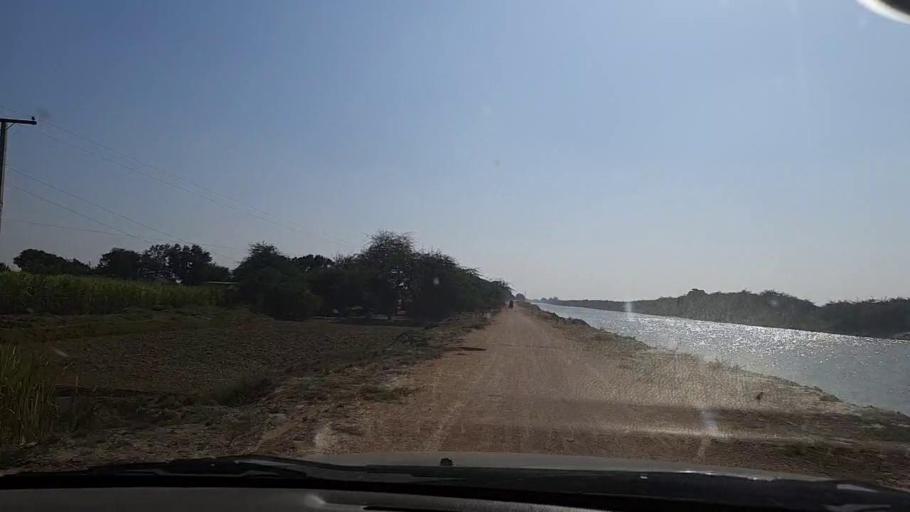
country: PK
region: Sindh
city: Thatta
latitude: 24.6028
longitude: 68.0507
